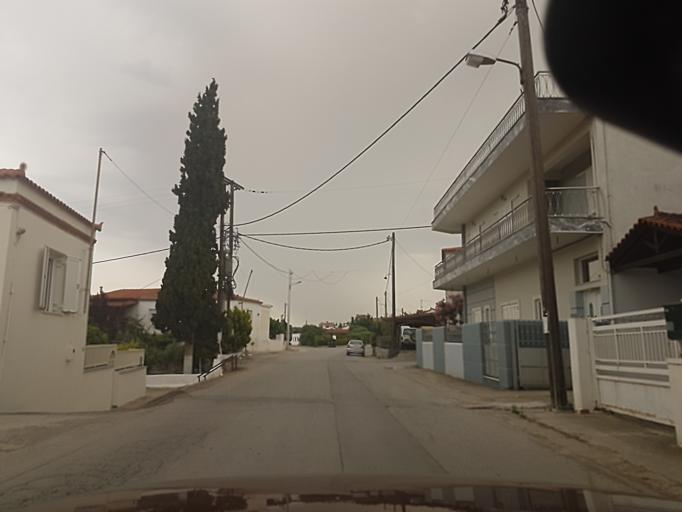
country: GR
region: Central Greece
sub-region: Nomos Evvoias
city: Vasilikon
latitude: 38.4298
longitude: 23.6710
